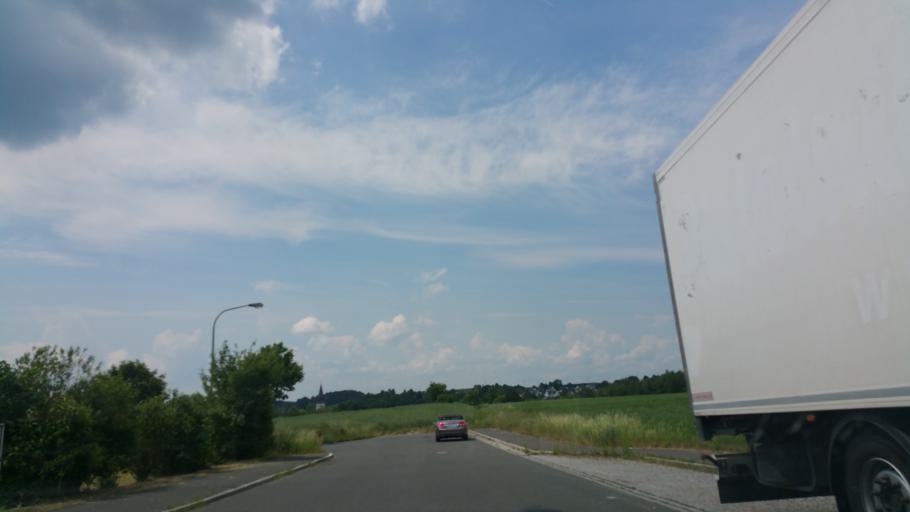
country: DE
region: Bavaria
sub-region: Upper Franconia
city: Schwarzenbach an der Saale
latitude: 50.2248
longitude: 11.9441
